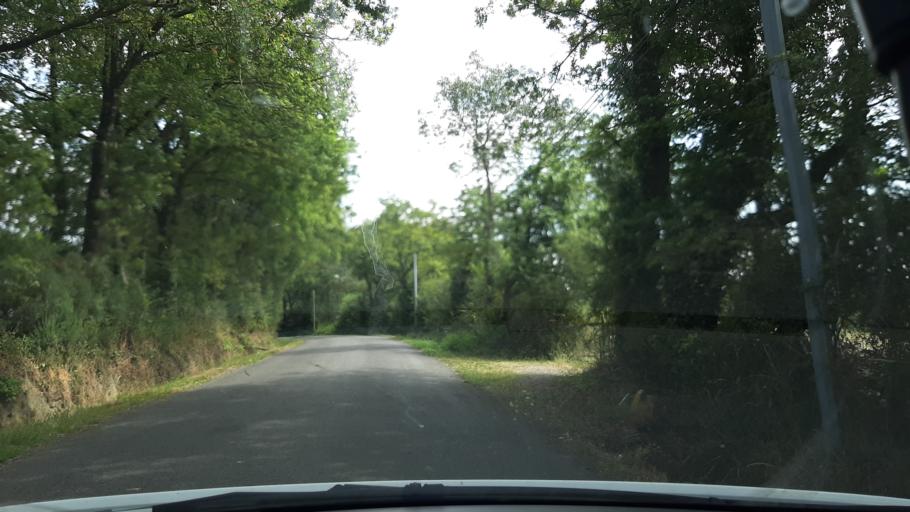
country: FR
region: Pays de la Loire
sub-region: Departement de la Vendee
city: Saint-Etienne-du-Bois
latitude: 46.7858
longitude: -1.5668
